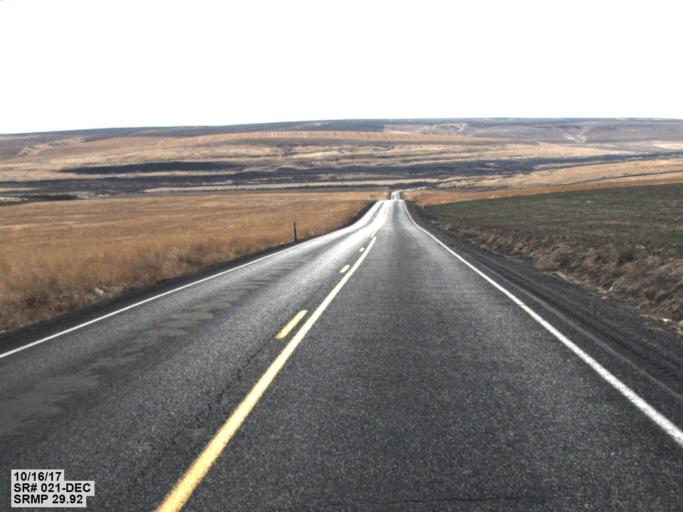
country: US
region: Washington
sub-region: Adams County
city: Ritzville
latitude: 46.9836
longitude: -118.6637
